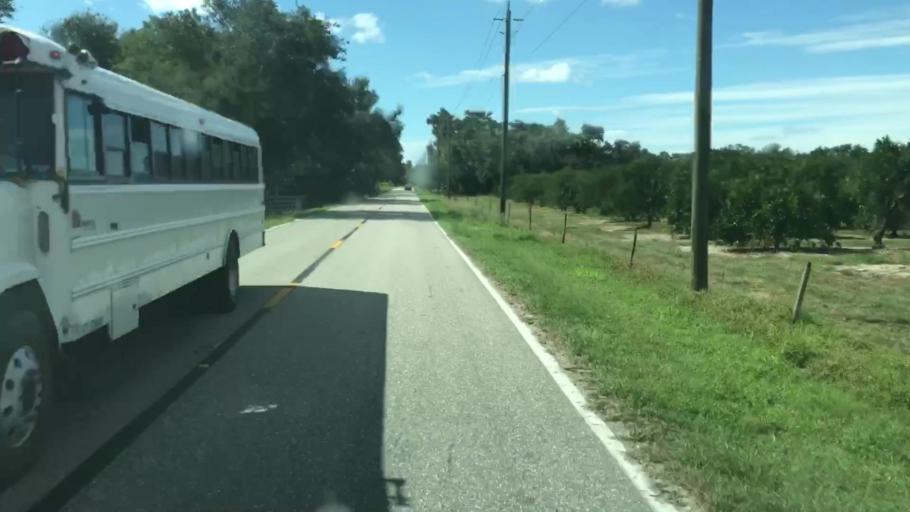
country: US
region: Florida
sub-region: Lee County
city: Alva
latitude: 26.7260
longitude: -81.6281
